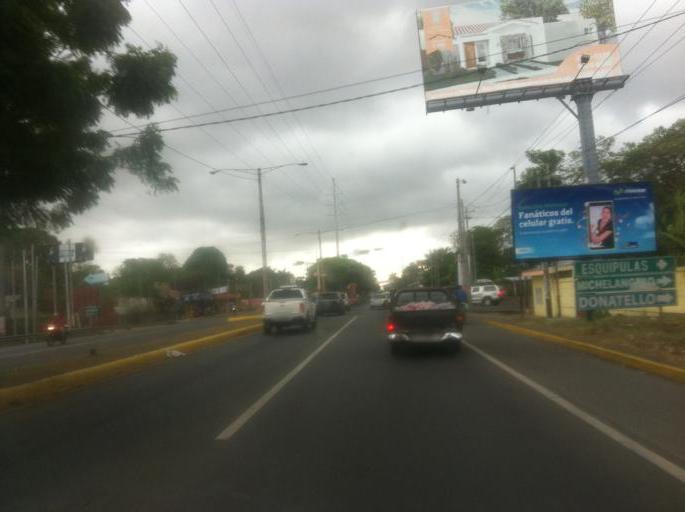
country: NI
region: Masaya
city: Ticuantepe
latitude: 12.0736
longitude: -86.2190
